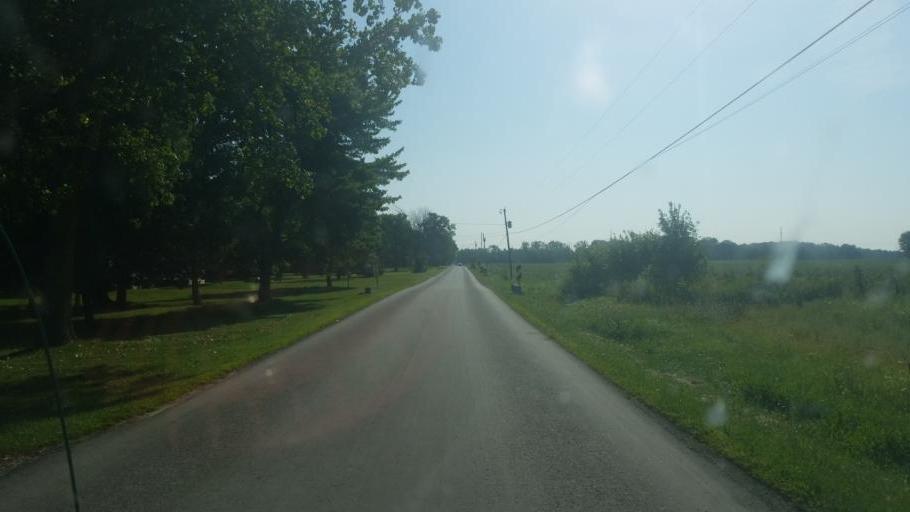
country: US
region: Ohio
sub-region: Wayne County
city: West Salem
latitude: 41.0855
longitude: -82.1278
